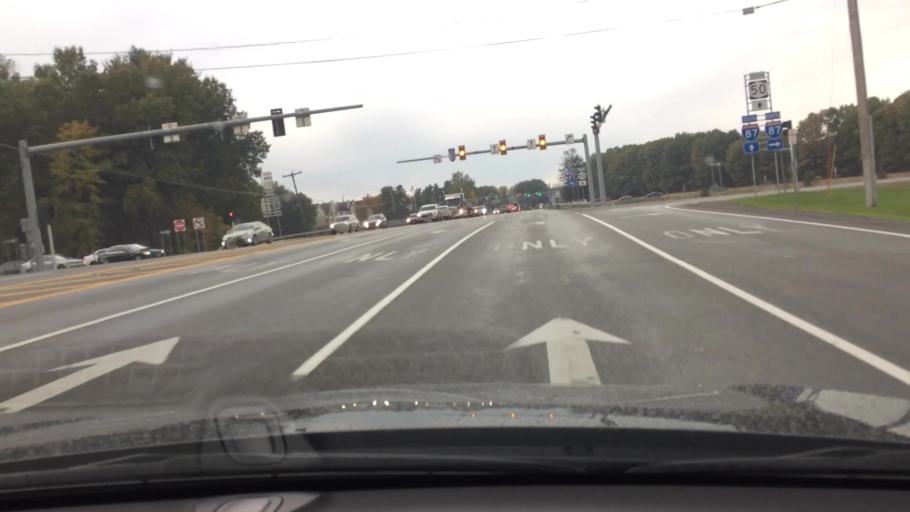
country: US
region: New York
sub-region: Saratoga County
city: Saratoga Springs
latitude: 43.0975
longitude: -73.7506
